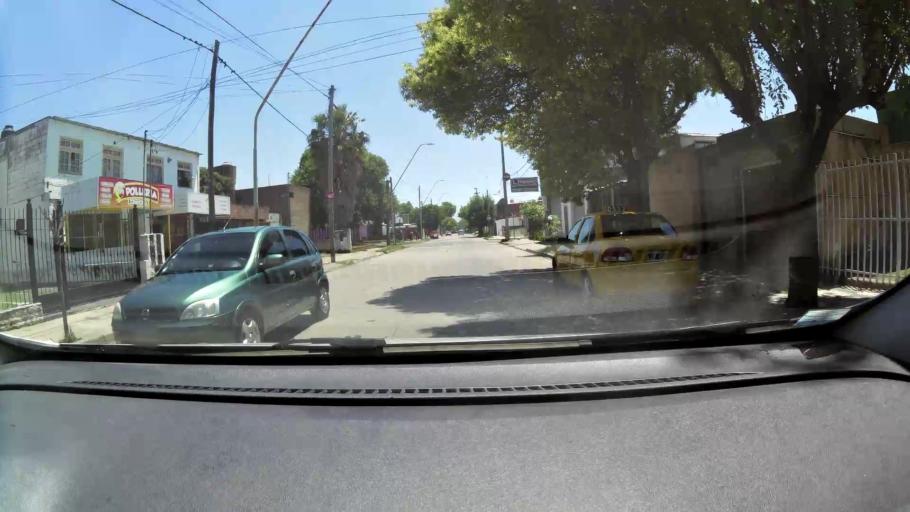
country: AR
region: Cordoba
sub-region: Departamento de Capital
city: Cordoba
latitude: -31.4152
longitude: -64.2316
